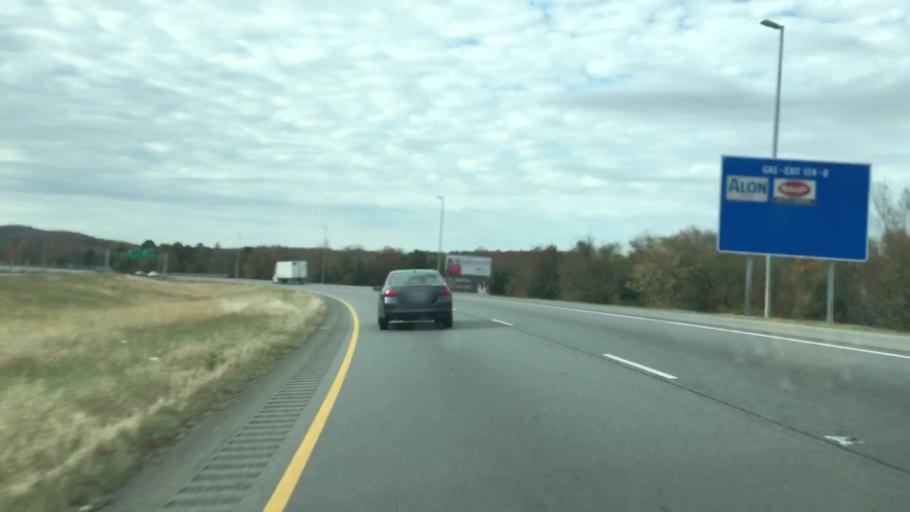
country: US
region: Arkansas
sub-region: Faulkner County
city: Conway
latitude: 35.1178
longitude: -92.4506
